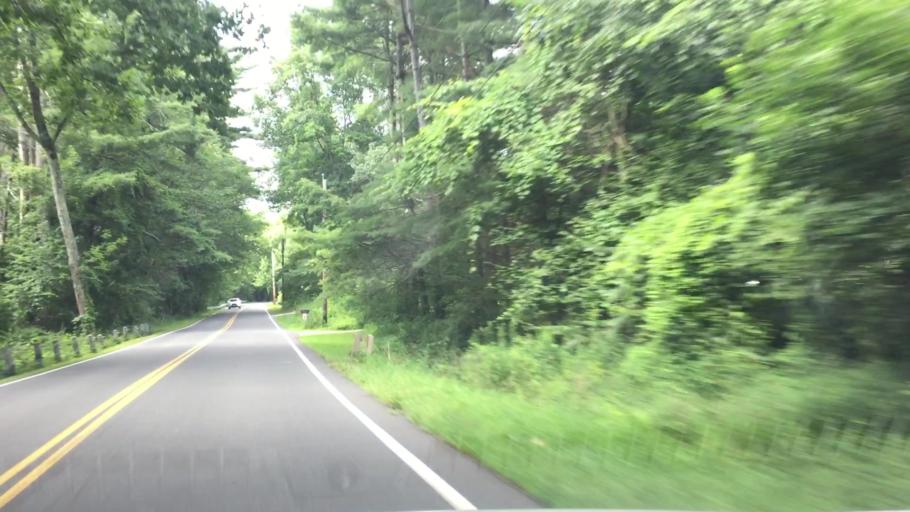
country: US
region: Massachusetts
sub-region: Berkshire County
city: Great Barrington
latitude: 42.2205
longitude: -73.4035
